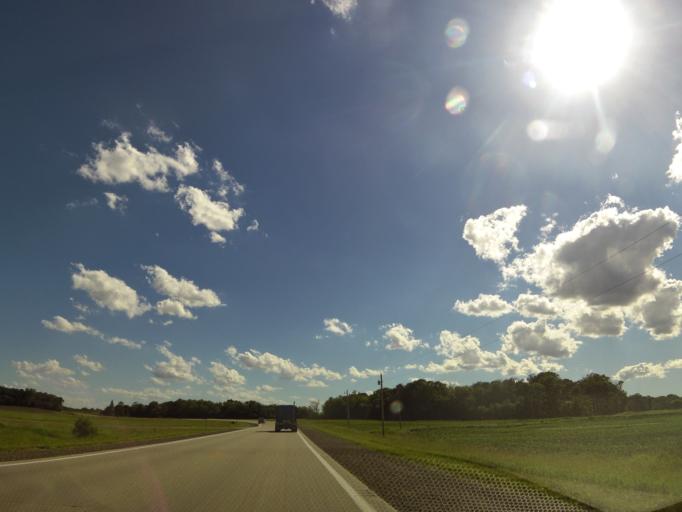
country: US
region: Minnesota
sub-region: McLeod County
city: Winsted
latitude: 44.9218
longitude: -94.1826
